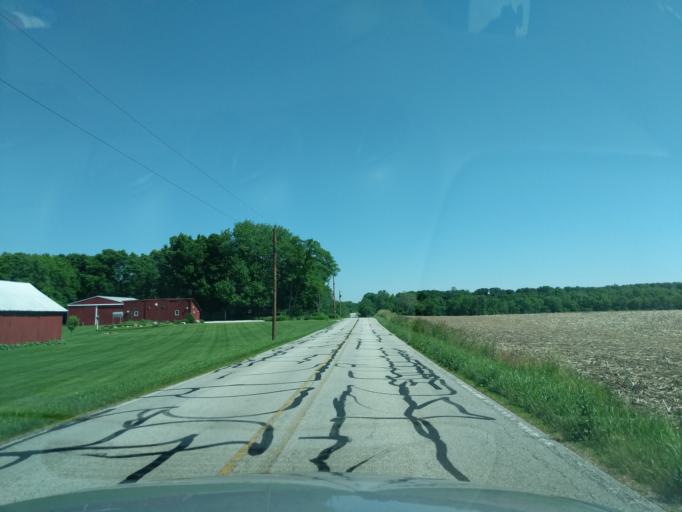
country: US
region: Indiana
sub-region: Huntington County
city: Warren
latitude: 40.7235
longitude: -85.5073
